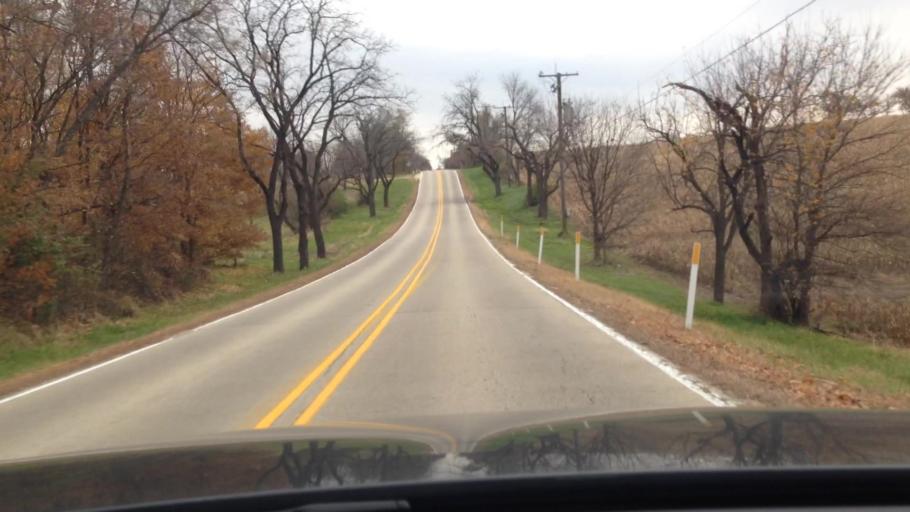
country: US
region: Illinois
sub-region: McHenry County
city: Woodstock
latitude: 42.2766
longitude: -88.4717
